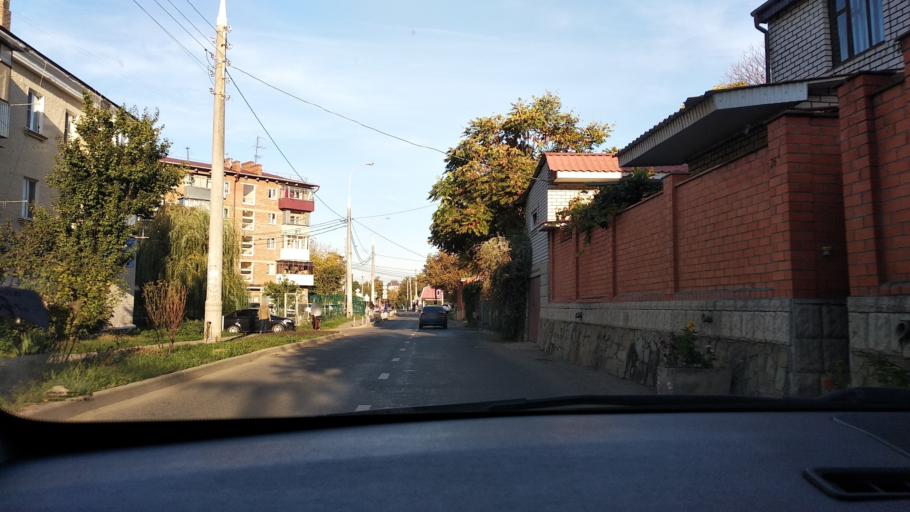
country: RU
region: Adygeya
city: Yablonovskiy
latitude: 45.0113
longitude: 38.9612
